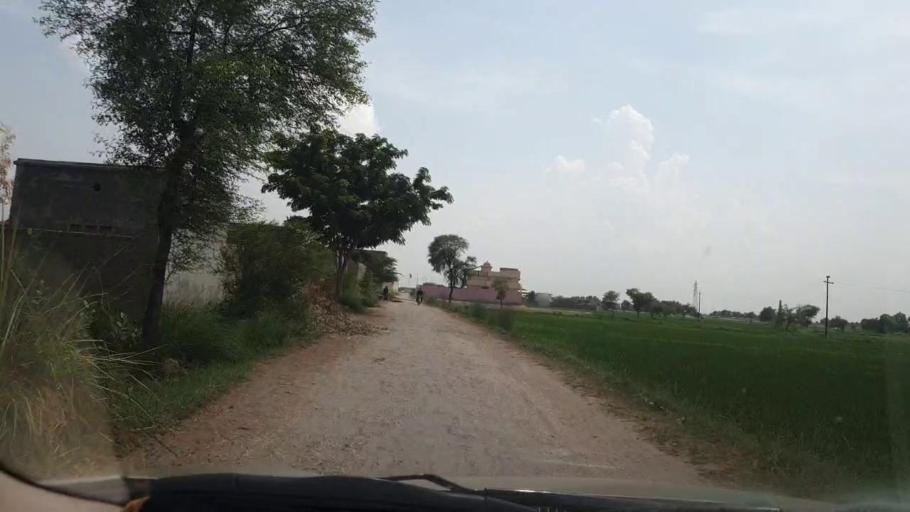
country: PK
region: Sindh
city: Larkana
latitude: 27.5777
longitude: 68.1645
